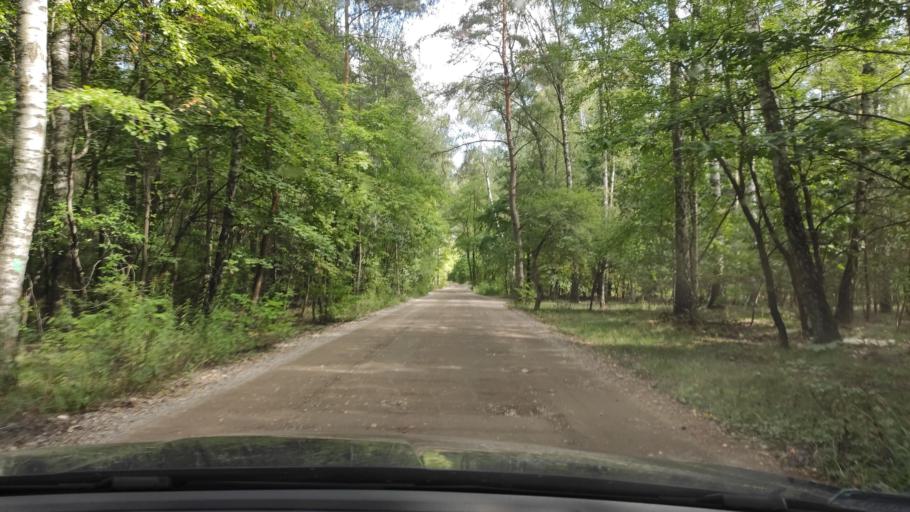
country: PL
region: Greater Poland Voivodeship
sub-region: Powiat poznanski
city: Swarzedz
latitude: 52.4160
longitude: 17.0324
